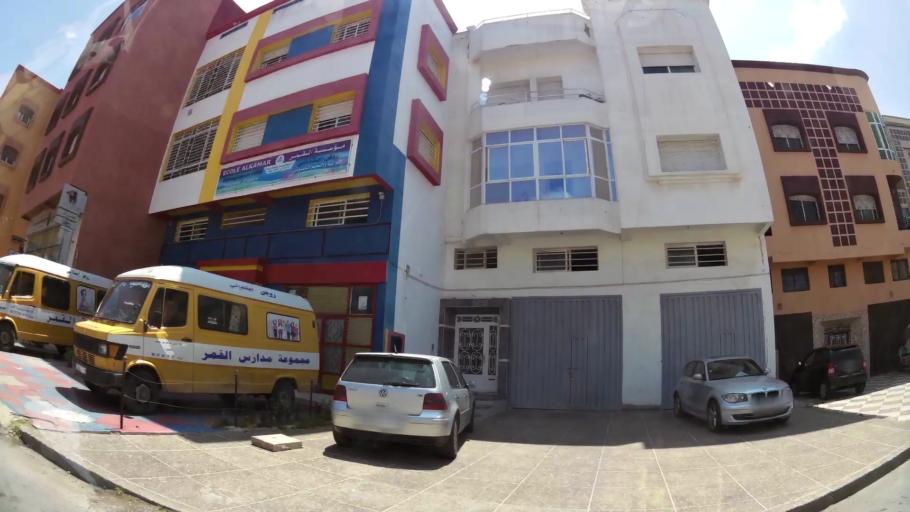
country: MA
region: Gharb-Chrarda-Beni Hssen
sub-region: Kenitra Province
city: Kenitra
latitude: 34.2692
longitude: -6.6115
